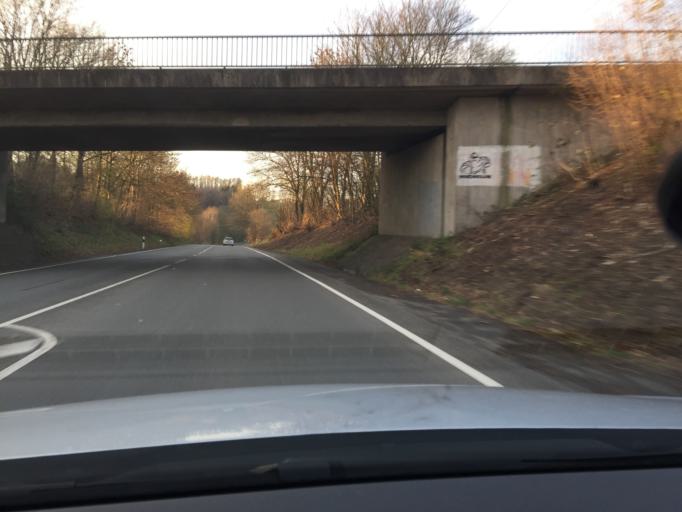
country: DE
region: North Rhine-Westphalia
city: Sprockhovel
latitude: 51.3308
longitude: 7.2248
